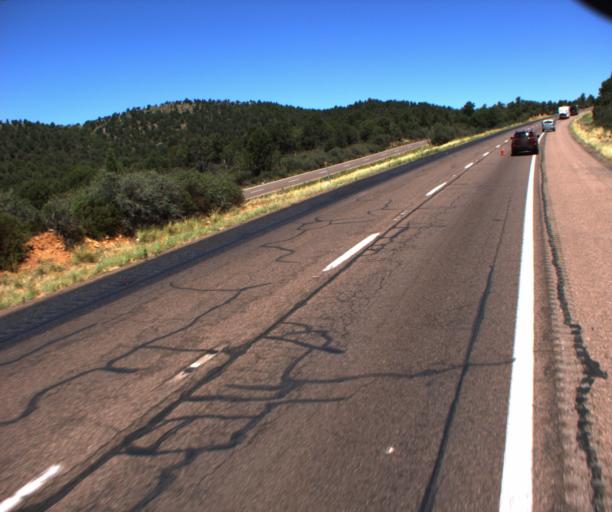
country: US
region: Arizona
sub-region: Gila County
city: Payson
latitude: 34.1996
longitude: -111.3302
